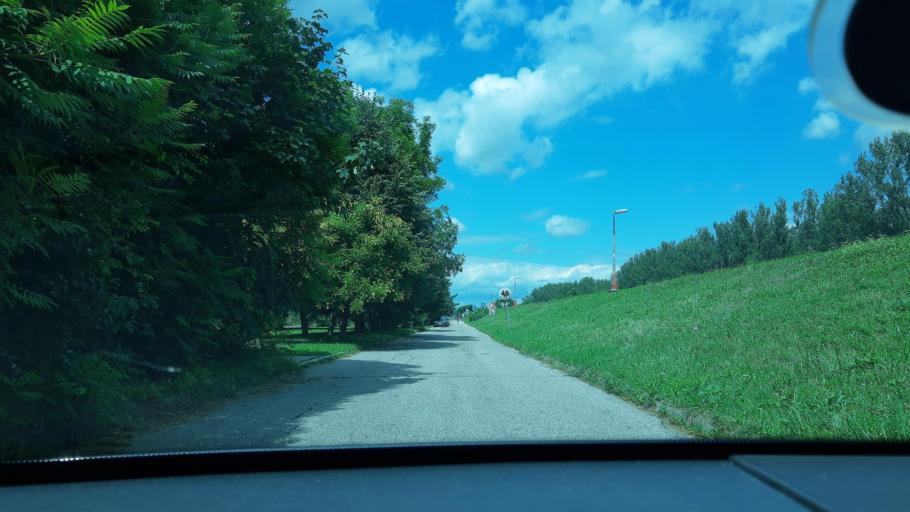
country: SK
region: Trnavsky
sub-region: Okres Trnava
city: Piestany
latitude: 48.5940
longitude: 17.8405
